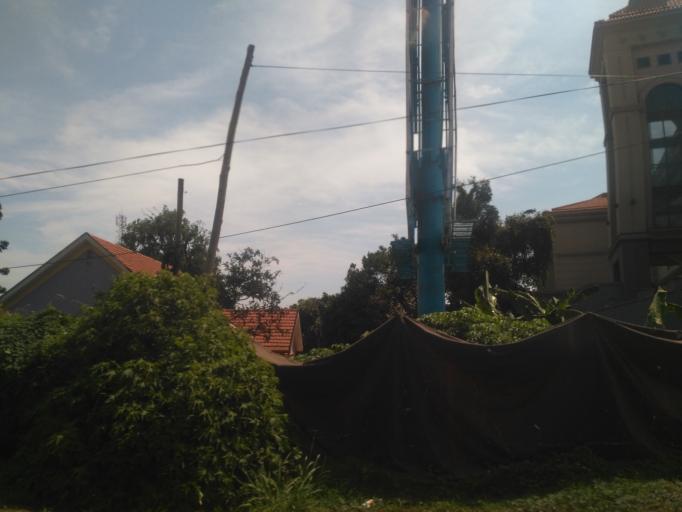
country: UG
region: Central Region
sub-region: Wakiso District
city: Entebbe
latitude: 0.0593
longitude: 32.4729
